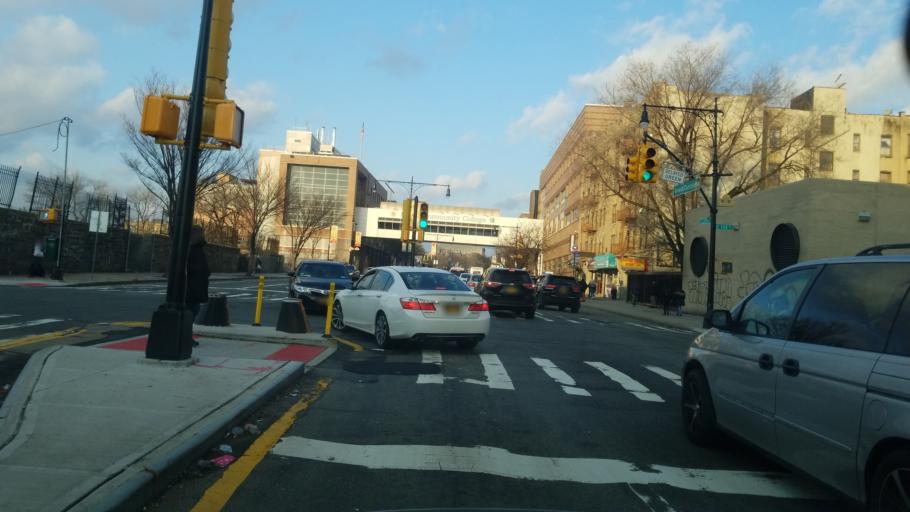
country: US
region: New Jersey
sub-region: Bergen County
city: Edgewater
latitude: 40.8164
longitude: -73.9283
